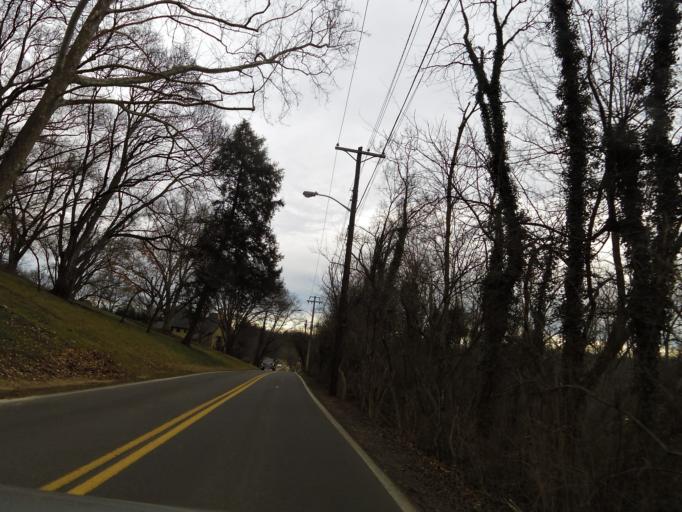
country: US
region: Tennessee
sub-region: Knox County
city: Knoxville
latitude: 35.9321
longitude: -83.9765
